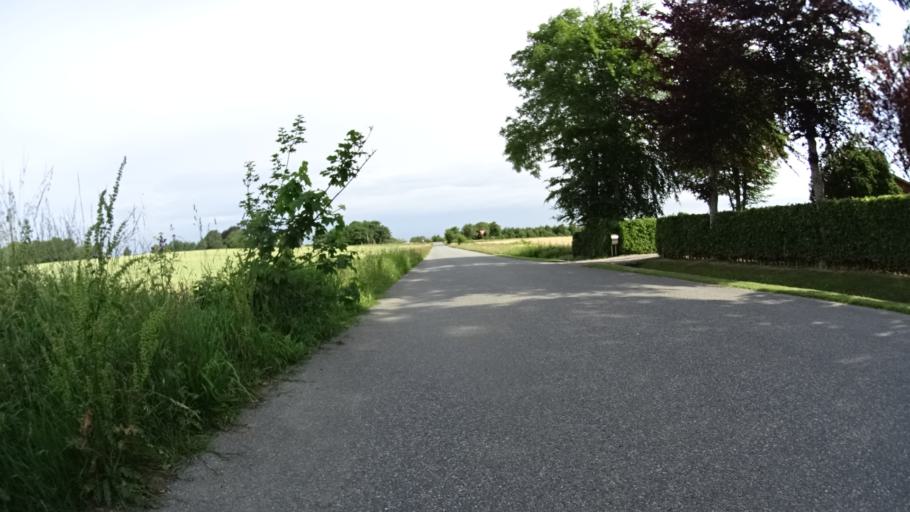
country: DK
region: Central Jutland
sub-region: Arhus Kommune
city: Kolt
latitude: 56.1268
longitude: 10.0801
